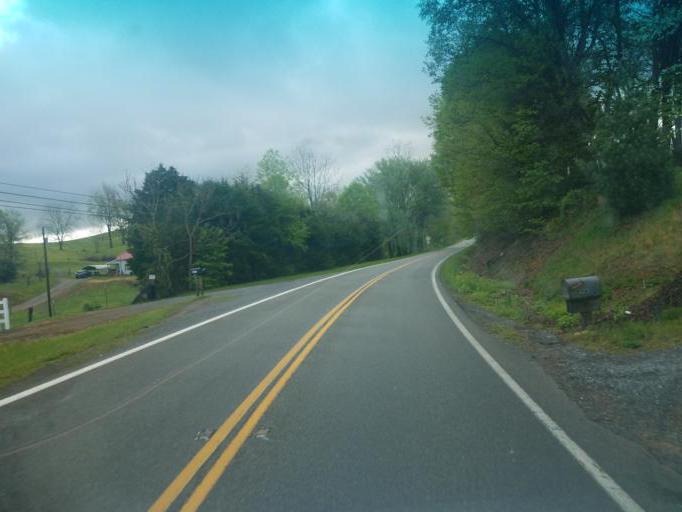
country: US
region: Virginia
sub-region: Washington County
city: Emory
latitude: 36.6560
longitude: -81.7969
